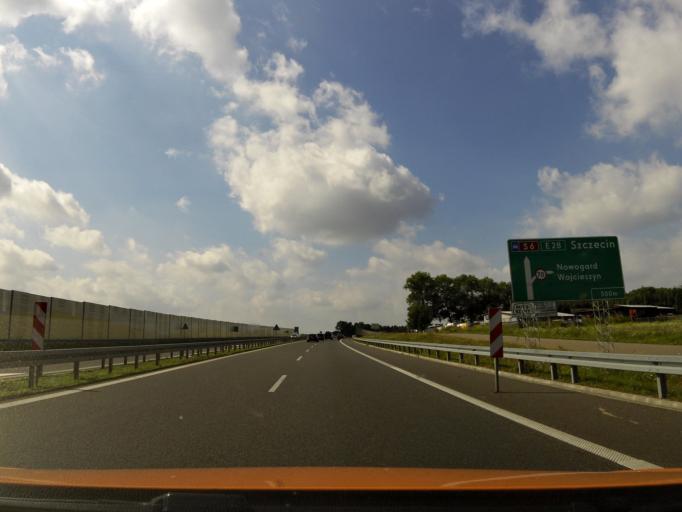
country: PL
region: West Pomeranian Voivodeship
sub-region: Powiat goleniowski
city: Nowogard
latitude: 53.6925
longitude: 15.1527
